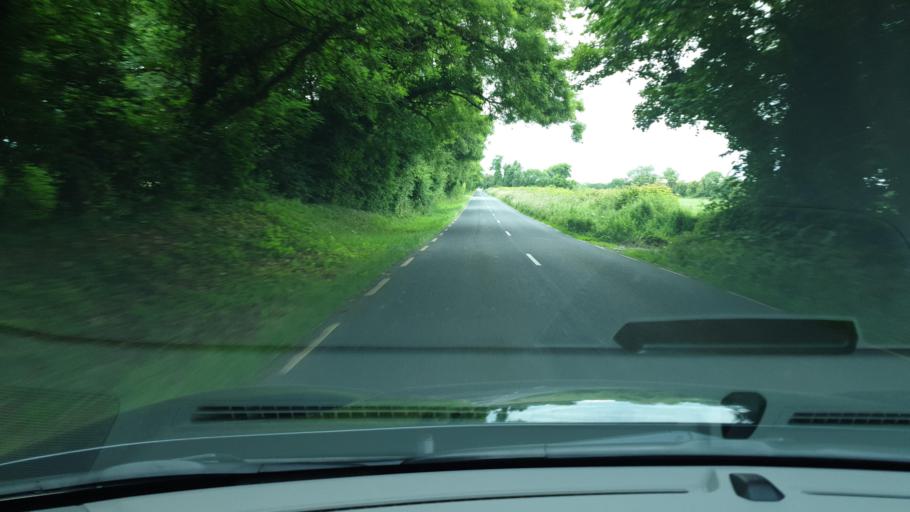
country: IE
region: Leinster
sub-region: An Mhi
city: Ratoath
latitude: 53.5157
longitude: -6.4700
